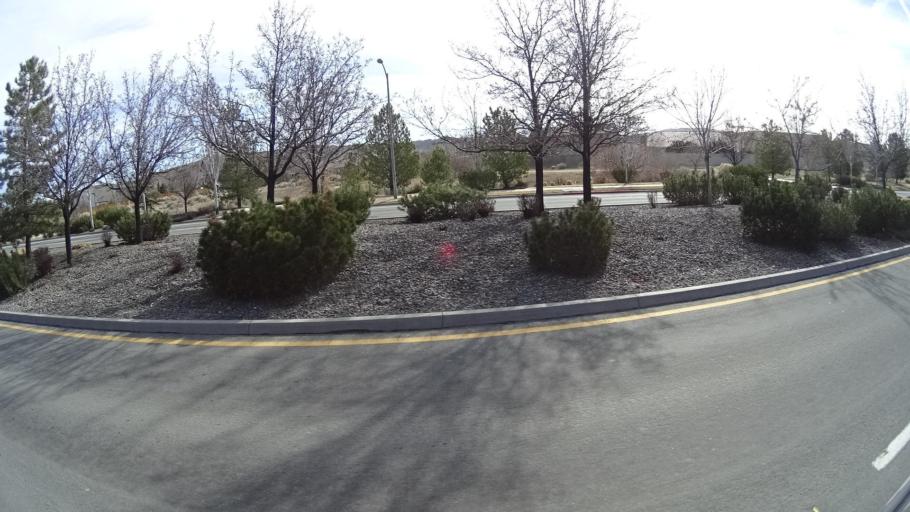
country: US
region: Nevada
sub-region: Washoe County
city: Sun Valley
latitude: 39.5847
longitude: -119.7244
